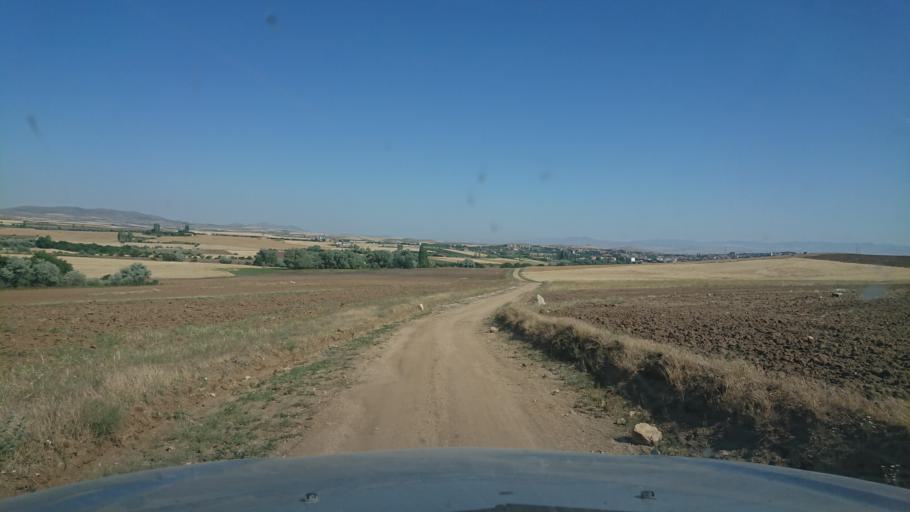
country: TR
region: Aksaray
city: Agacoren
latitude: 38.8490
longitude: 33.9163
